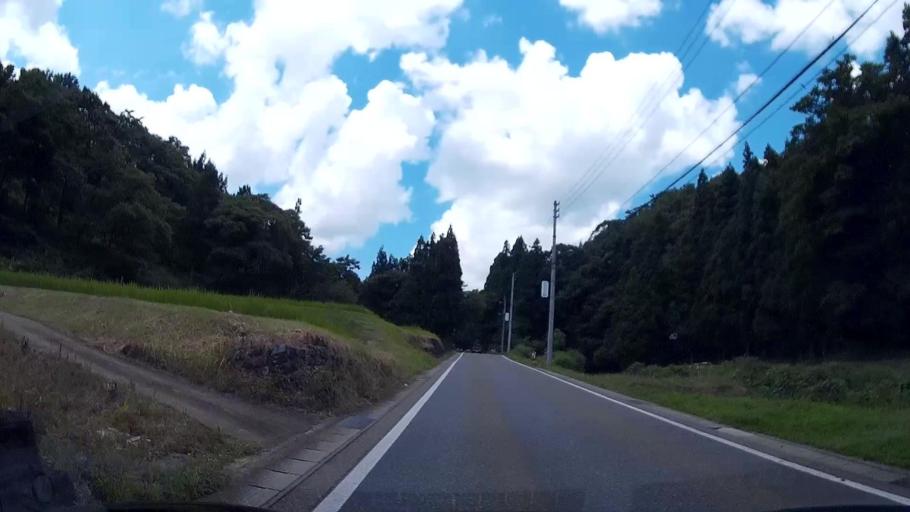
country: JP
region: Niigata
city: Shiozawa
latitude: 37.0192
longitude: 138.8181
